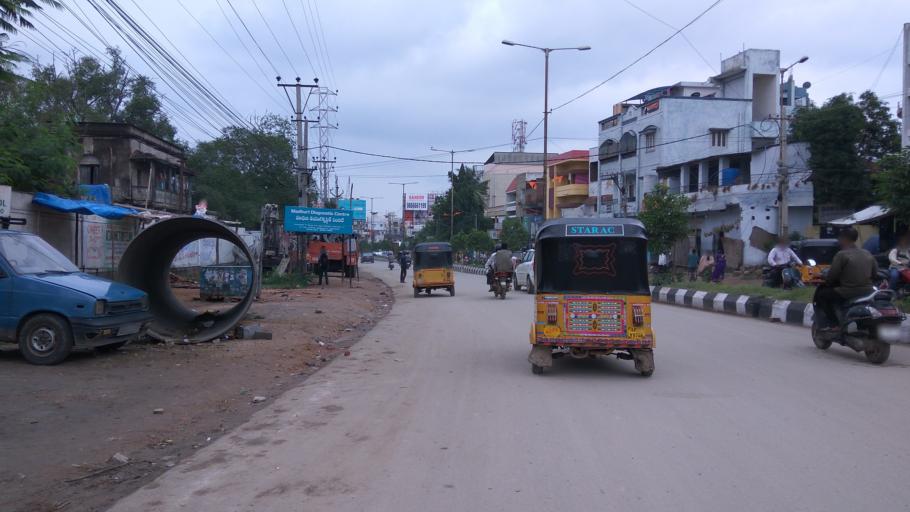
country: IN
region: Telangana
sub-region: Hyderabad
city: Malkajgiri
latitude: 17.4605
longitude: 78.5355
